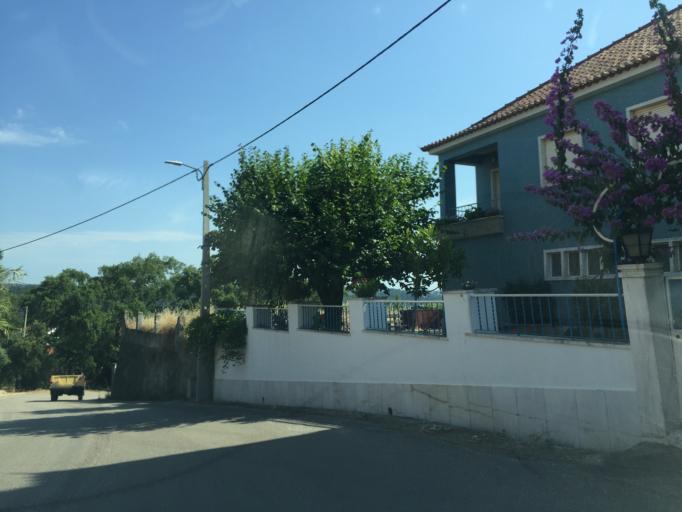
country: PT
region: Santarem
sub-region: Ferreira do Zezere
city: Ferreira do Zezere
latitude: 39.6053
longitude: -8.2890
